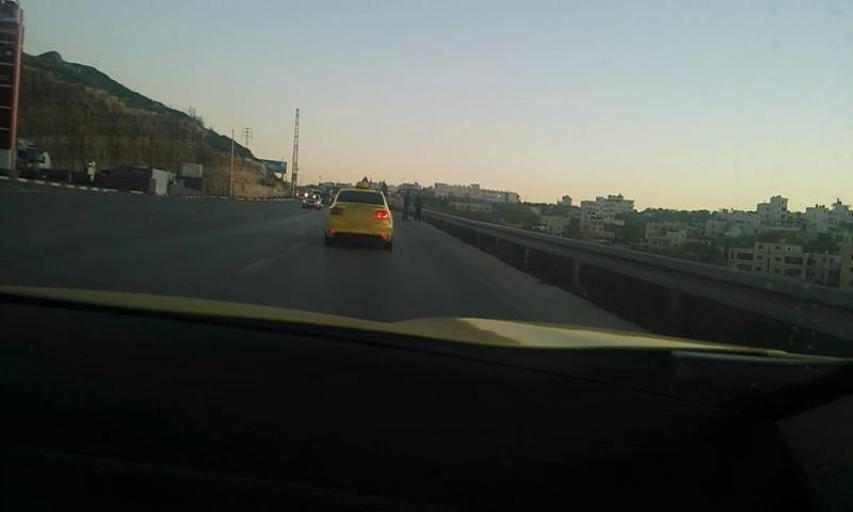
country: PS
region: West Bank
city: Jifna
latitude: 31.9501
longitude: 35.2151
